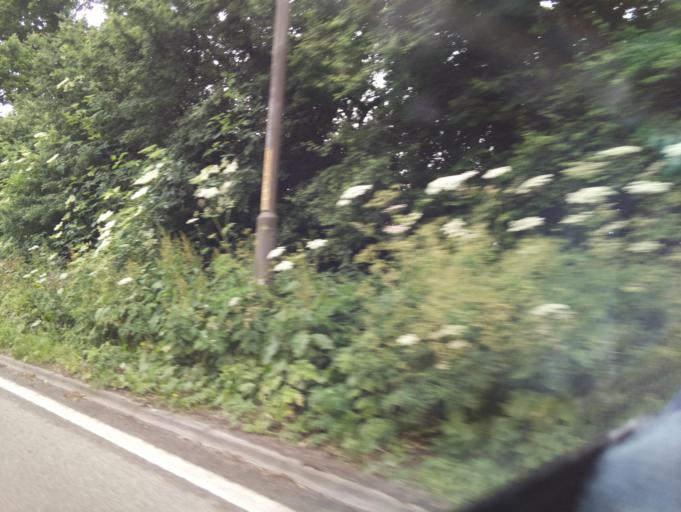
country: GB
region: England
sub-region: Derbyshire
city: Ashbourne
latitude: 53.0038
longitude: -1.7140
